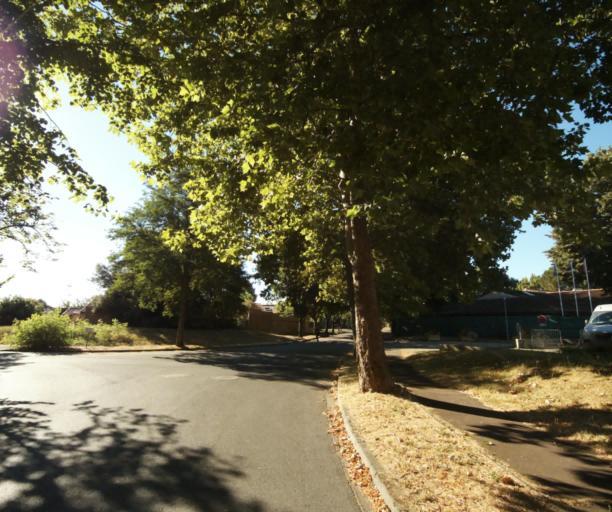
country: FR
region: Midi-Pyrenees
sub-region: Departement de la Haute-Garonne
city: Castanet-Tolosan
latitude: 43.5241
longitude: 1.5047
